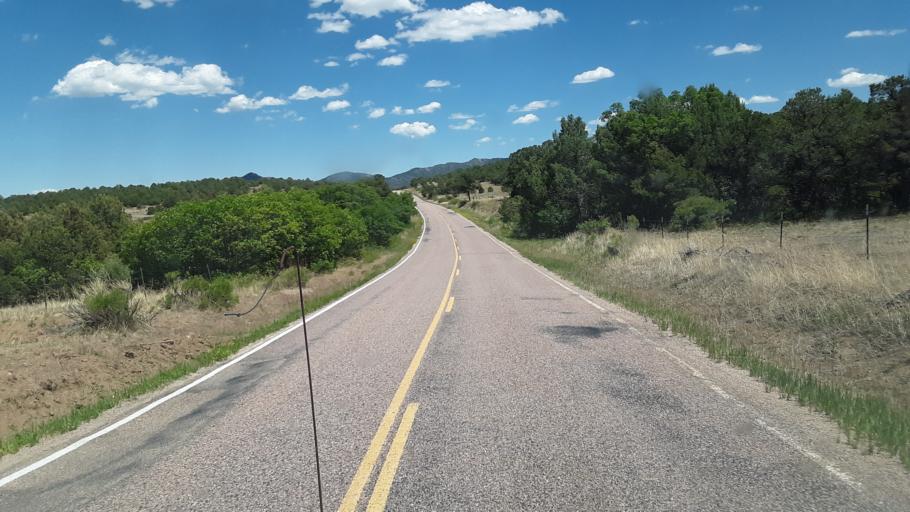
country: US
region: Colorado
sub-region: Custer County
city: Westcliffe
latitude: 38.3101
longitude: -105.6444
